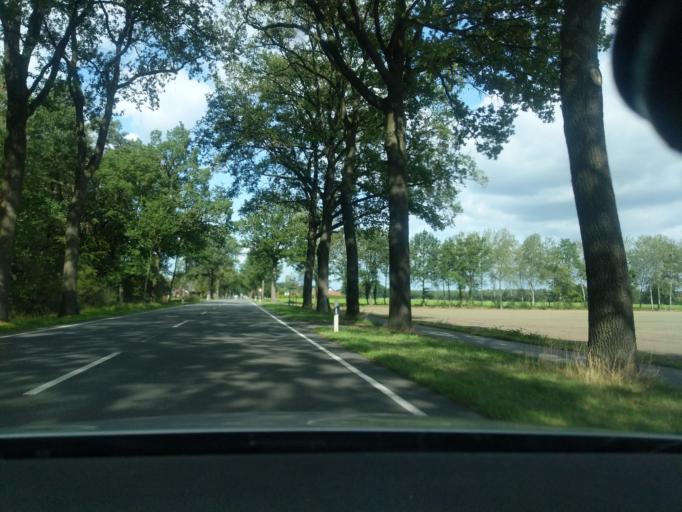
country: DE
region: Lower Saxony
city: Bohmte
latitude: 52.3878
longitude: 8.3105
